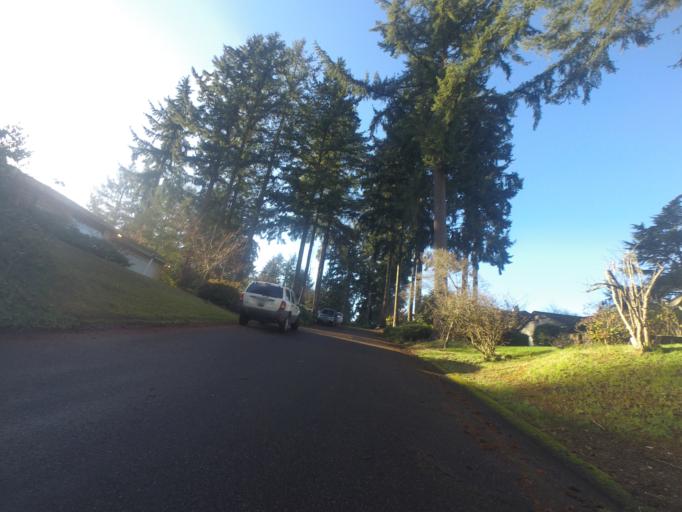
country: US
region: Washington
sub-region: Pierce County
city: Fircrest
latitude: 47.2268
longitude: -122.5299
